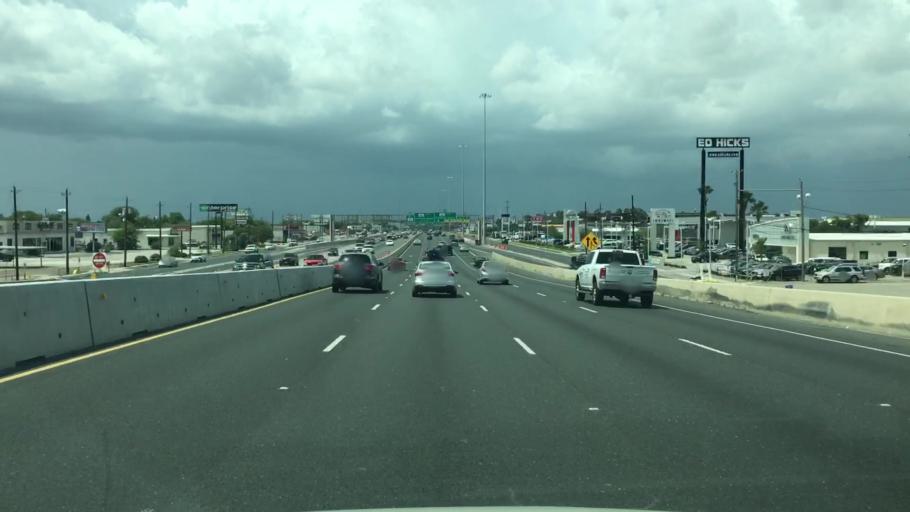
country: US
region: Texas
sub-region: Nueces County
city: Corpus Christi
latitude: 27.7294
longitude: -97.4144
